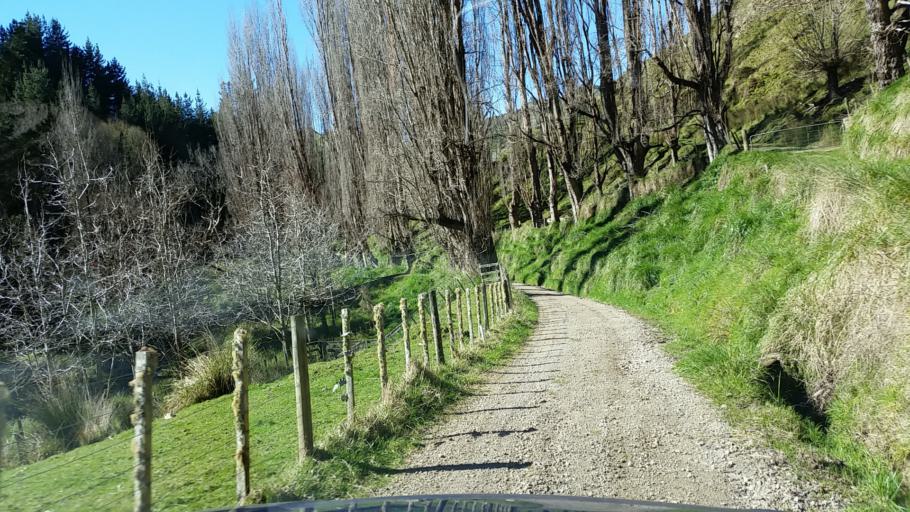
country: NZ
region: Taranaki
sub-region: South Taranaki District
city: Patea
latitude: -39.6208
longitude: 174.8265
